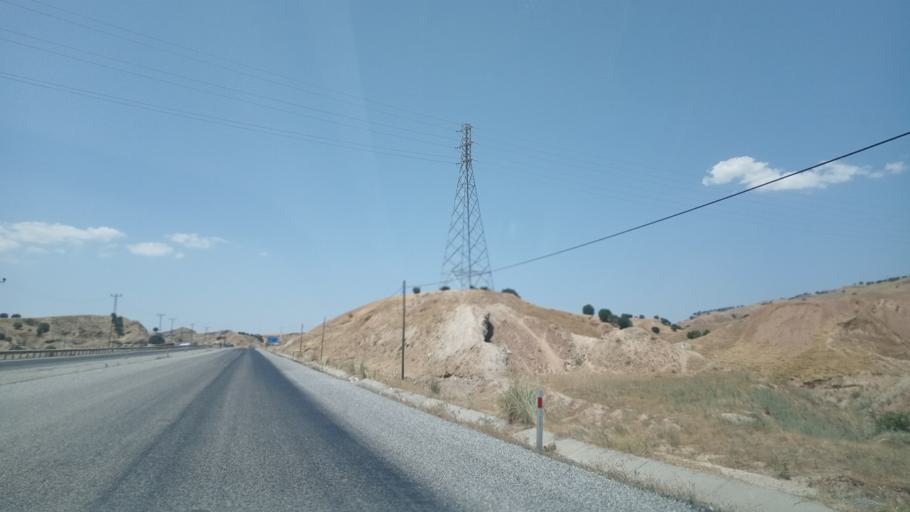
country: TR
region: Batman
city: Kozluk
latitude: 38.1682
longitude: 41.4770
